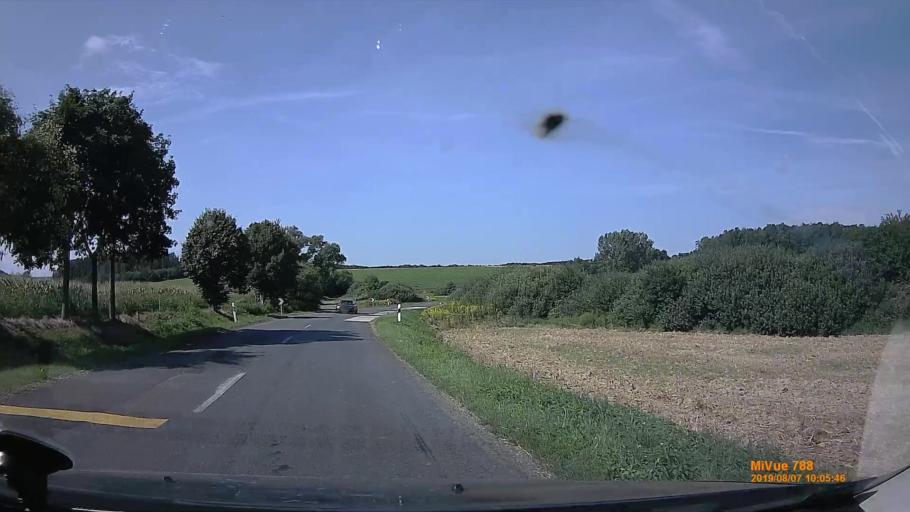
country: HU
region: Zala
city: Zalaegerszeg
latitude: 46.6946
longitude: 16.7499
